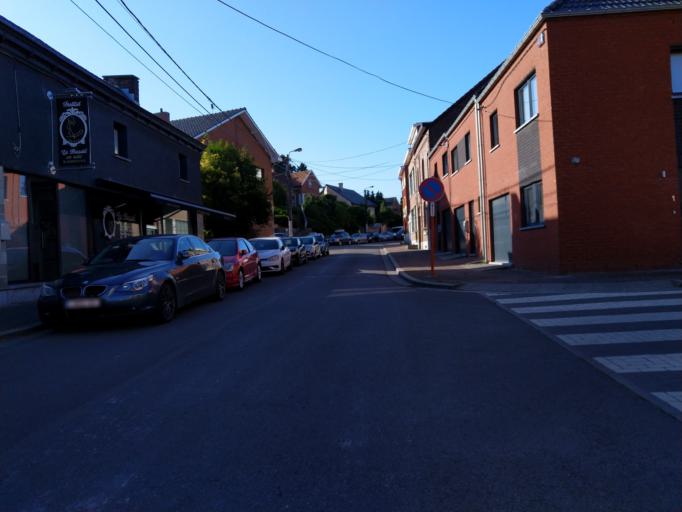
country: BE
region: Wallonia
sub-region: Province du Hainaut
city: Estinnes-au-Val
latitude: 50.4558
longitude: 4.1000
